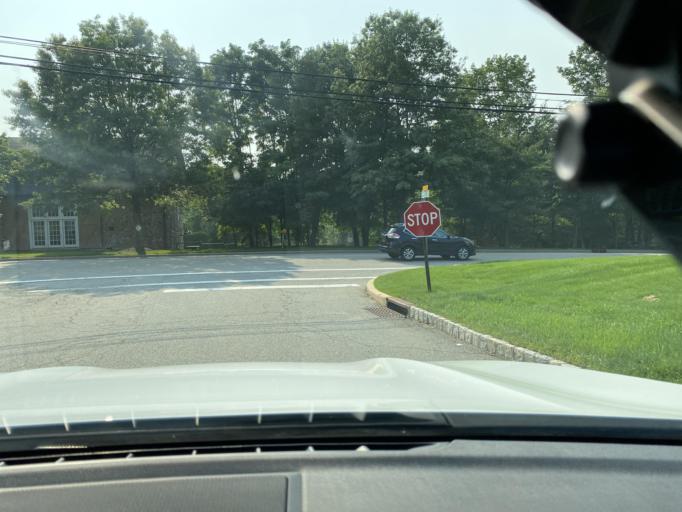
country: US
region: New Jersey
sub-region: Bergen County
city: Mahwah
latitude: 41.0850
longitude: -74.1268
